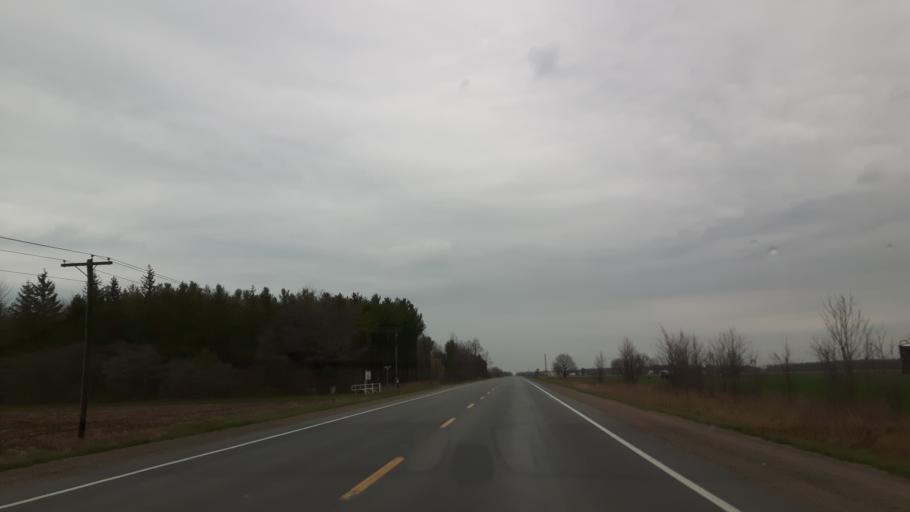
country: CA
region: Ontario
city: Goderich
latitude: 43.6195
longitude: -81.7056
